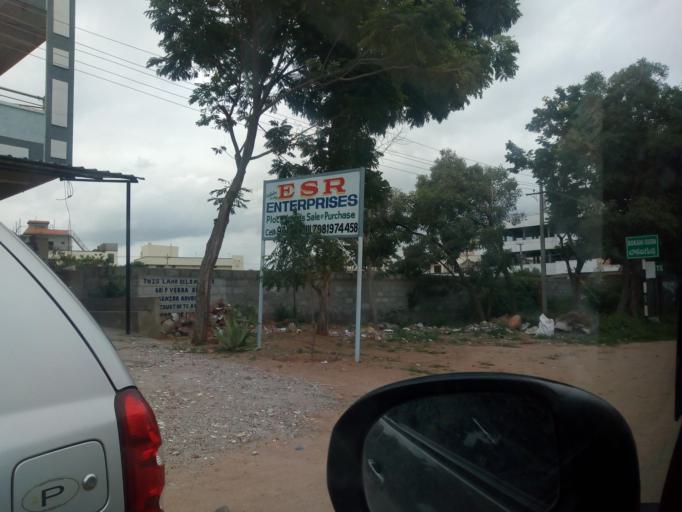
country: IN
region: Telangana
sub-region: Rangareddi
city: Ghatkesar
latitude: 17.4426
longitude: 78.6966
